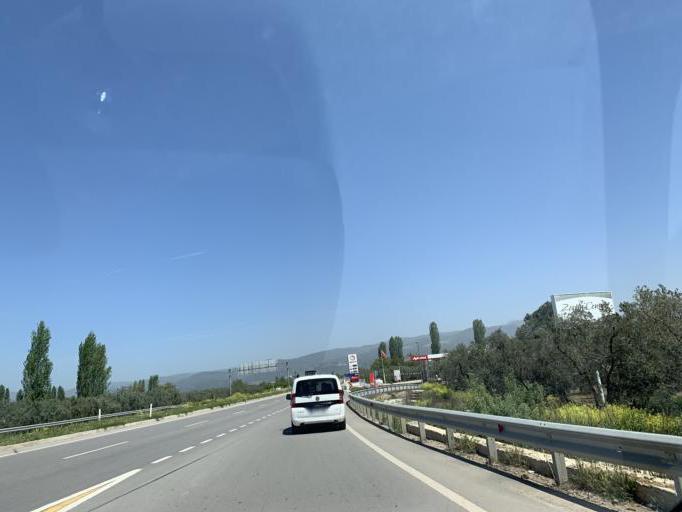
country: TR
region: Bursa
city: Iznik
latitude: 40.3977
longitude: 29.6941
